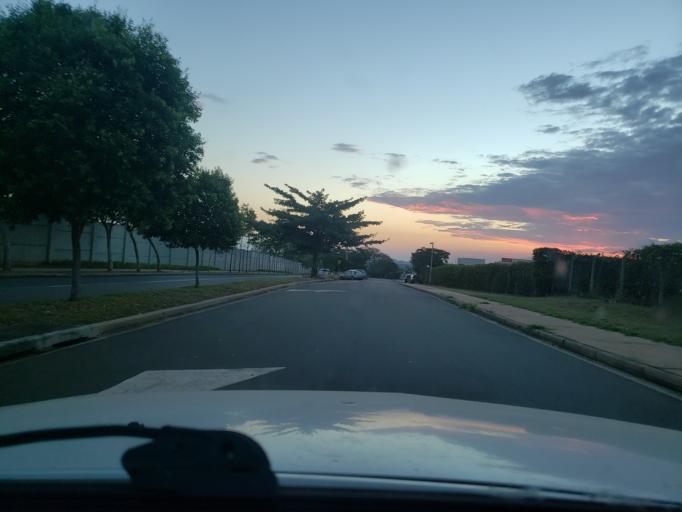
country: BR
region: Sao Paulo
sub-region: Mogi-Mirim
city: Mogi Mirim
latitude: -22.4892
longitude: -46.9779
